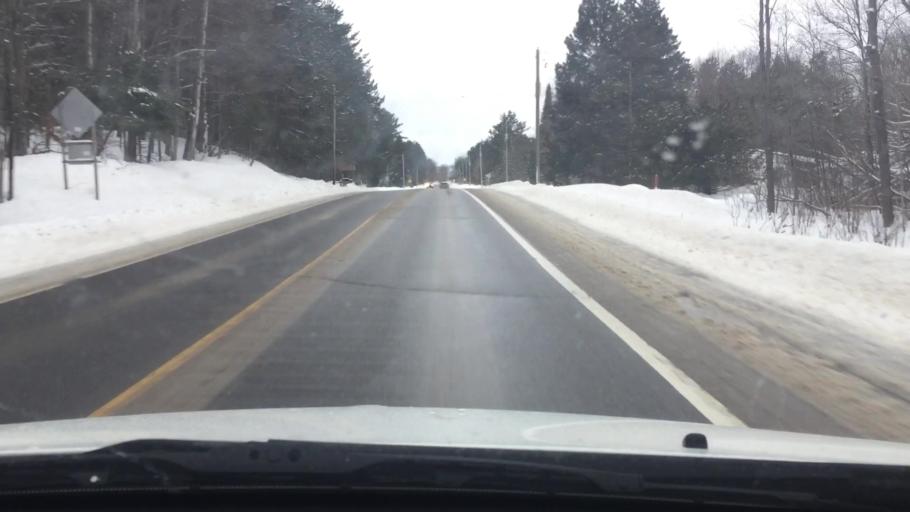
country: US
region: Michigan
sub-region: Charlevoix County
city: East Jordan
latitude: 45.1325
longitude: -85.0847
